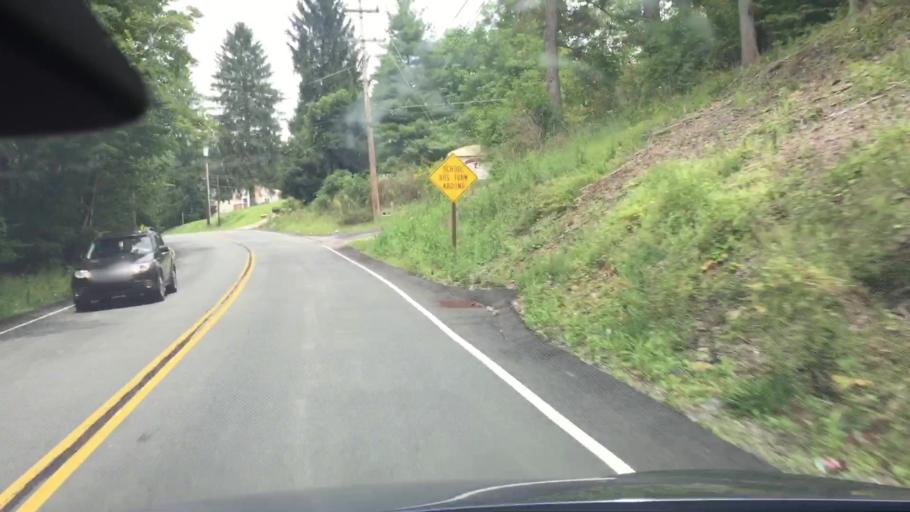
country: US
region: Pennsylvania
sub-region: Allegheny County
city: Monroeville
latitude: 40.4301
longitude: -79.7763
